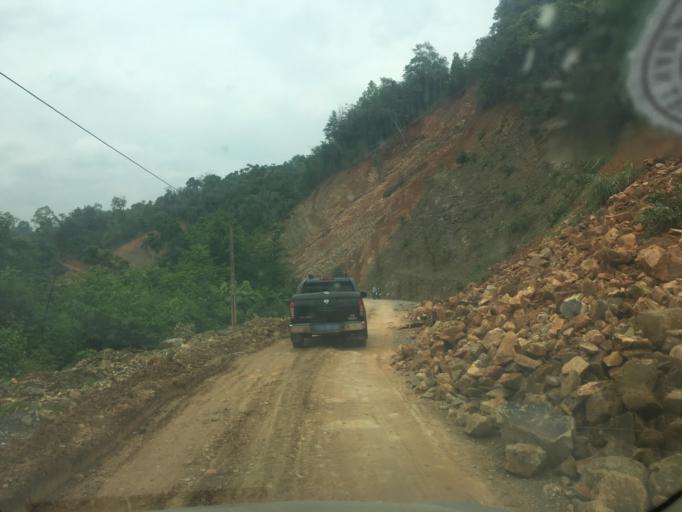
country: VN
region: Lang Son
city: Binh Gia
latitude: 22.1308
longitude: 106.3502
